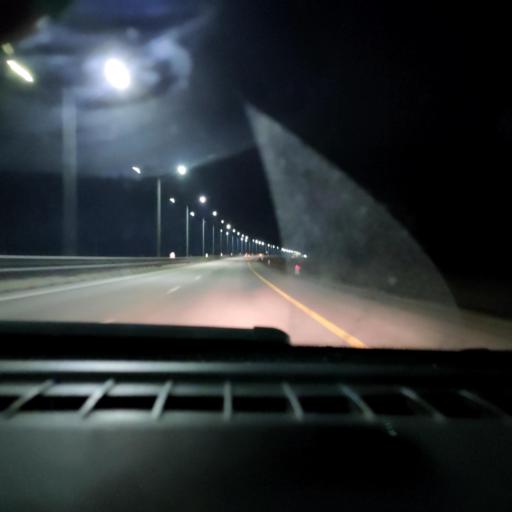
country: RU
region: Voronezj
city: Podkletnoye
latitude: 51.5795
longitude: 39.4632
